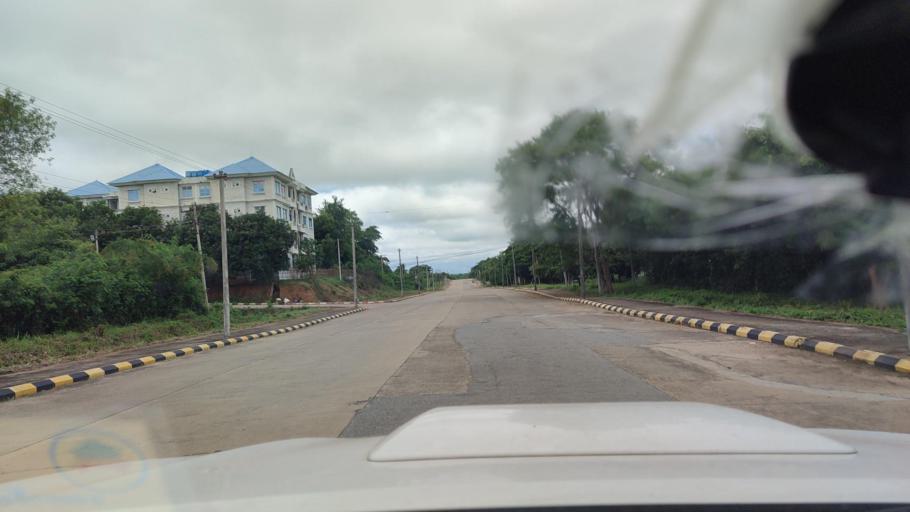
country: MM
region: Mandalay
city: Nay Pyi Taw
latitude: 19.7368
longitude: 96.0643
